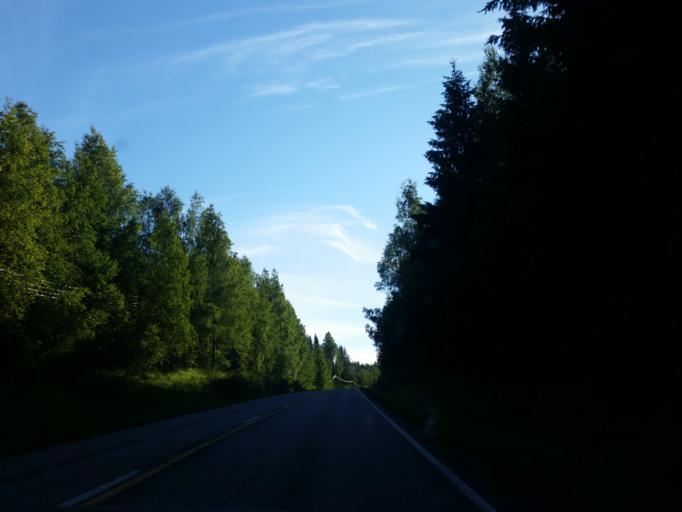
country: FI
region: Northern Savo
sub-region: Kuopio
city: Kuopio
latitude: 62.8443
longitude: 27.4198
